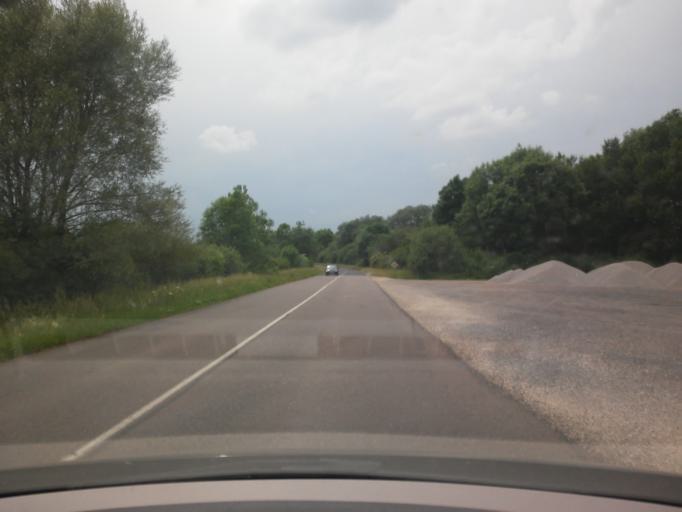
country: FR
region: Lorraine
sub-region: Departement de la Meuse
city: Vigneulles-les-Hattonchatel
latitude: 48.8424
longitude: 5.7421
